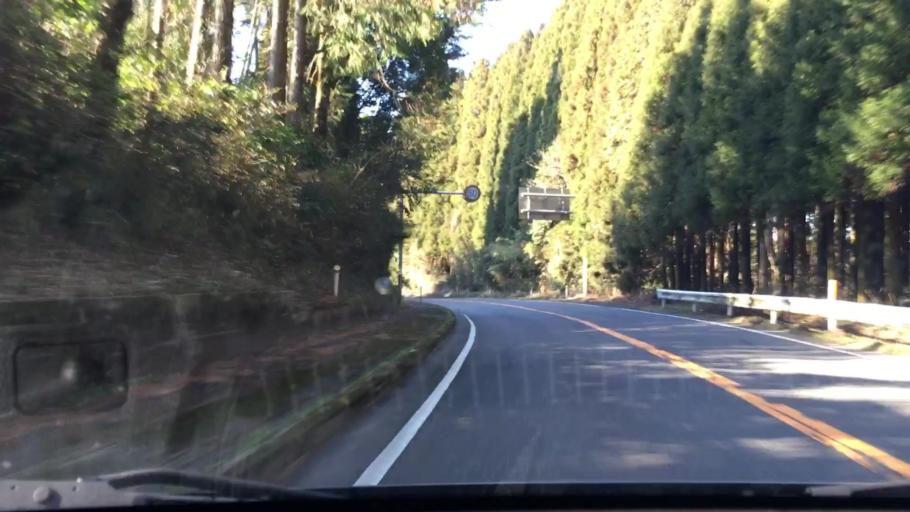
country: JP
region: Kagoshima
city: Sueyoshicho-ninokata
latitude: 31.6738
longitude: 130.9253
